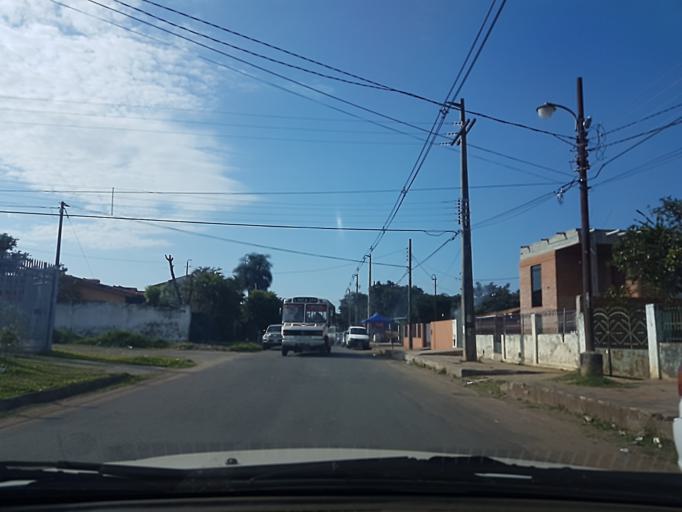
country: PY
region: Central
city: Colonia Mariano Roque Alonso
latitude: -25.2488
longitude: -57.5348
